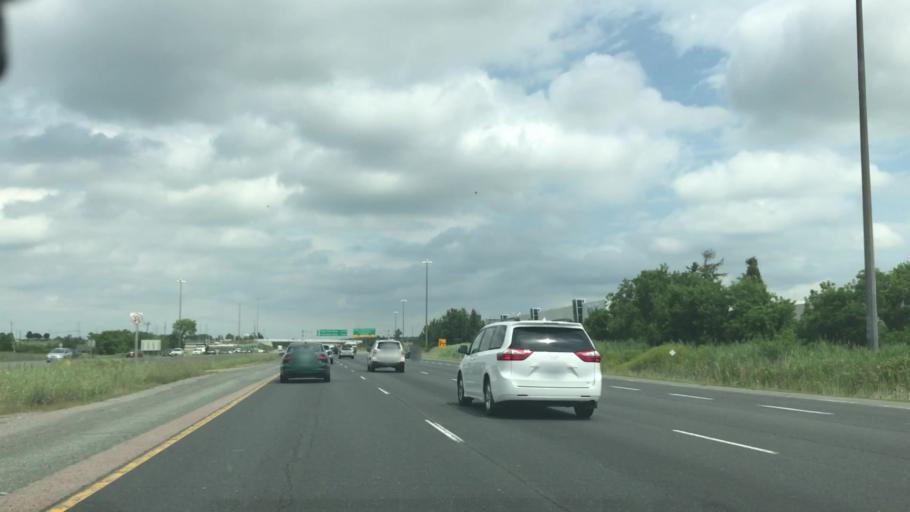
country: CA
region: Ontario
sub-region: York
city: Richmond Hill
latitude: 43.8760
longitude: -79.3775
